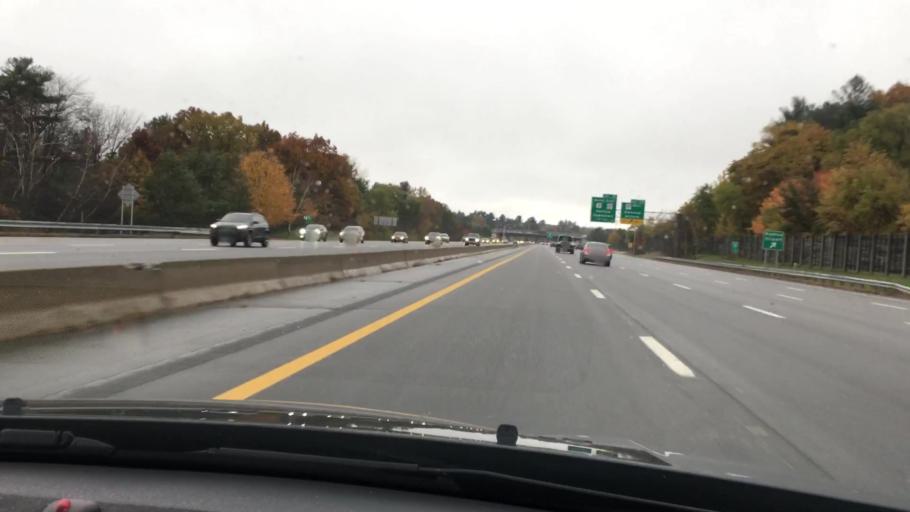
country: US
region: New Hampshire
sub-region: Hillsborough County
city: Nashua
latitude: 42.7832
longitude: -71.4944
